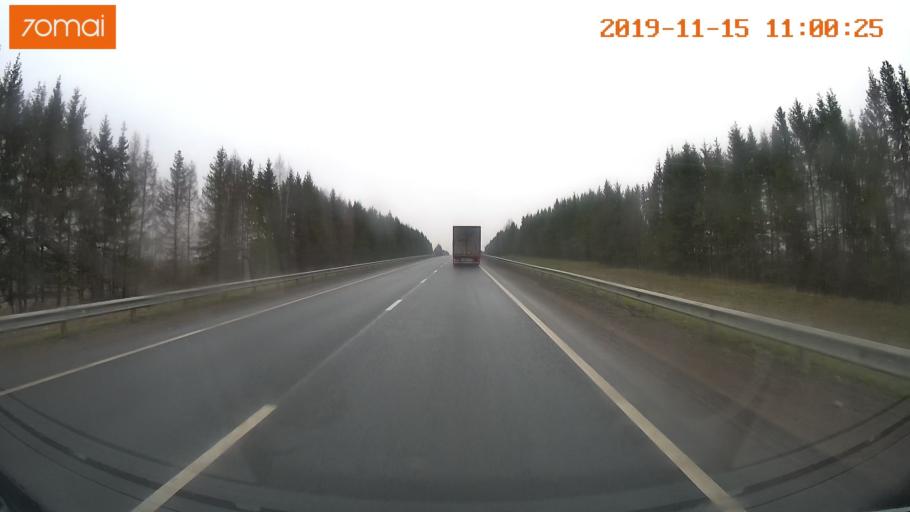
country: RU
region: Vologda
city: Chebsara
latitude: 59.1373
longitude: 38.8989
